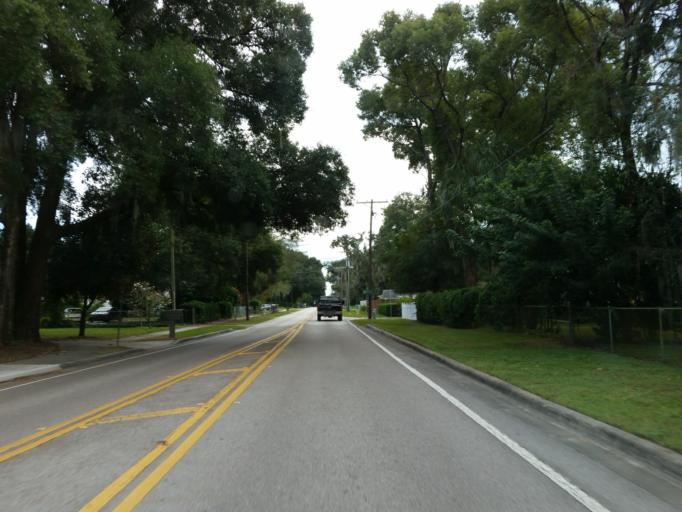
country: US
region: Florida
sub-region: Hillsborough County
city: Brandon
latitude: 27.9307
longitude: -82.2776
